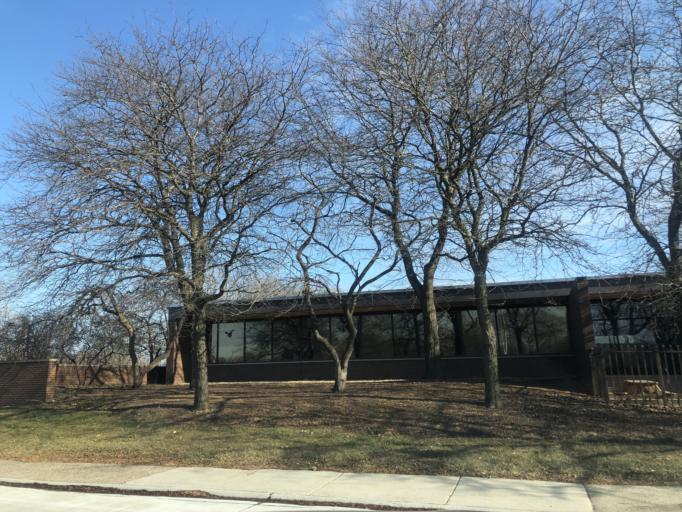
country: US
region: Illinois
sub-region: Cook County
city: Stickney
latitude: 41.8210
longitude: -87.7729
